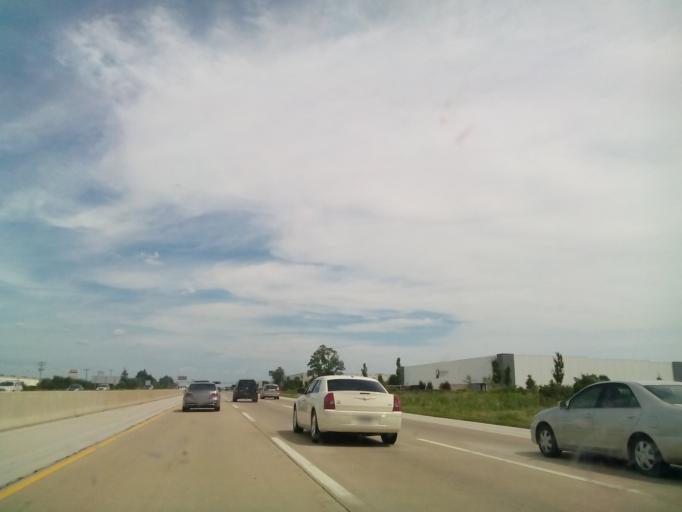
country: US
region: Illinois
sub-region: Kane County
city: North Aurora
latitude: 41.7950
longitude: -88.3638
